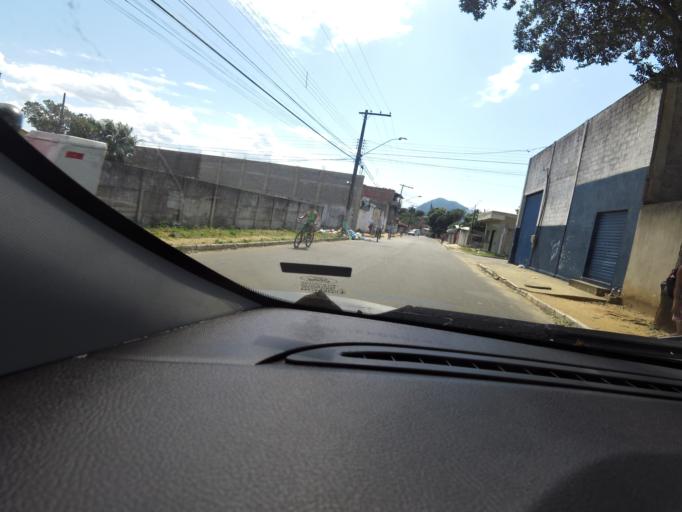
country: BR
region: Espirito Santo
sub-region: Guarapari
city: Guarapari
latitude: -20.6641
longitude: -40.5126
